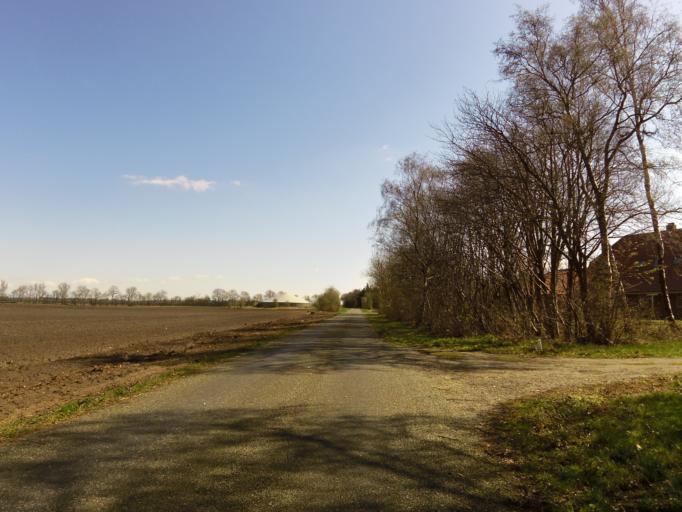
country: DK
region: South Denmark
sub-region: Esbjerg Kommune
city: Ribe
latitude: 55.3406
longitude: 8.8625
